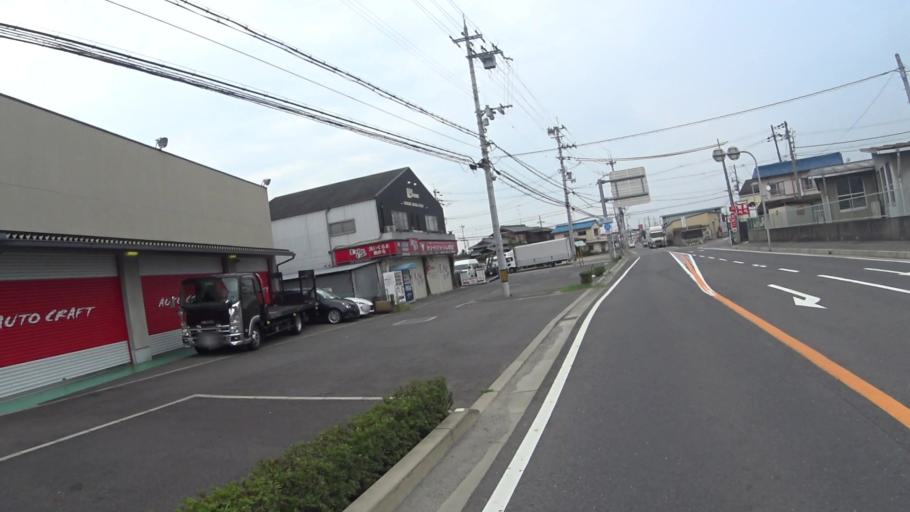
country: JP
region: Kyoto
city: Tanabe
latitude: 34.8502
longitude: 135.7455
